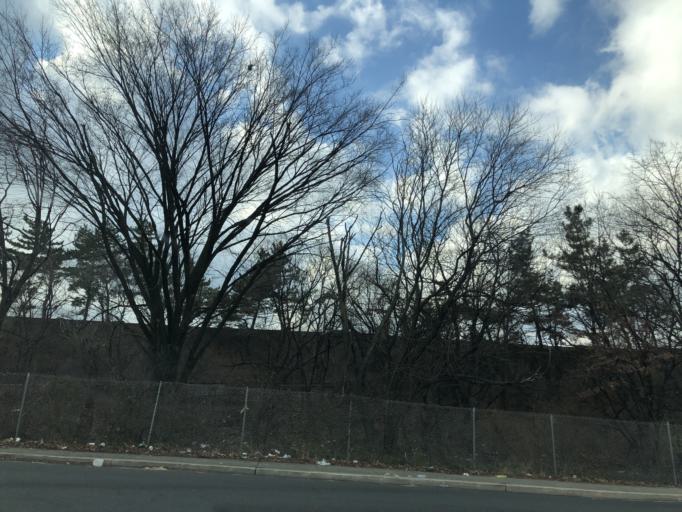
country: US
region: New Jersey
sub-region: Camden County
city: Camden
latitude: 39.9134
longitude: -75.1151
